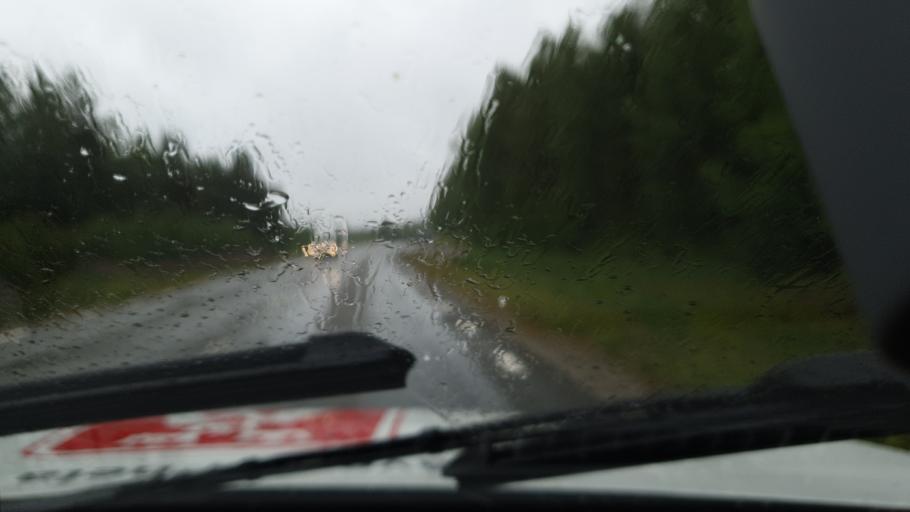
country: SE
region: Vaesterbotten
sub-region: Lycksele Kommun
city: Lycksele
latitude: 64.5578
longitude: 18.5197
